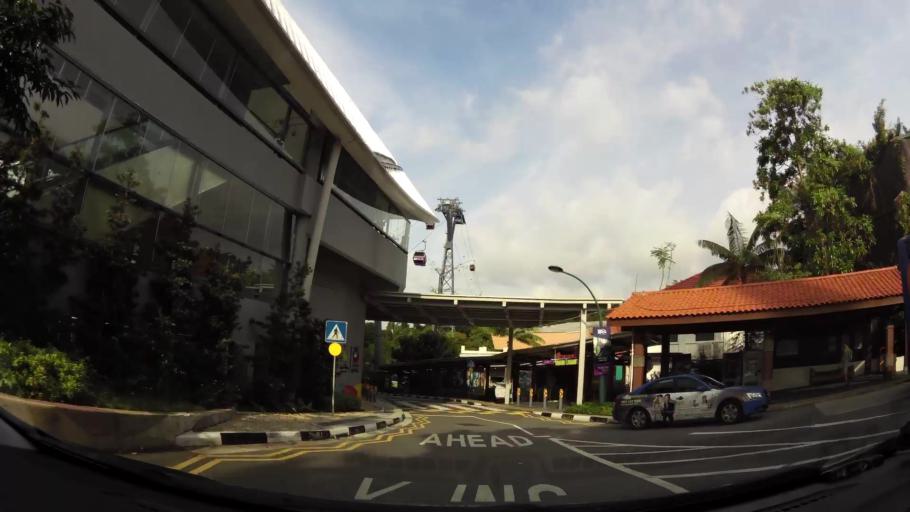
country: SG
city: Singapore
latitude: 1.2551
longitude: 103.8170
